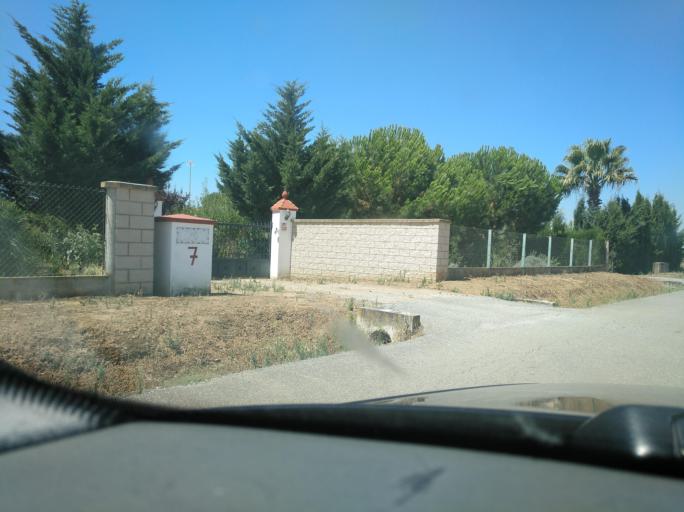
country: ES
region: Extremadura
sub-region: Provincia de Badajoz
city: Olivenza
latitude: 38.7291
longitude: -7.2186
